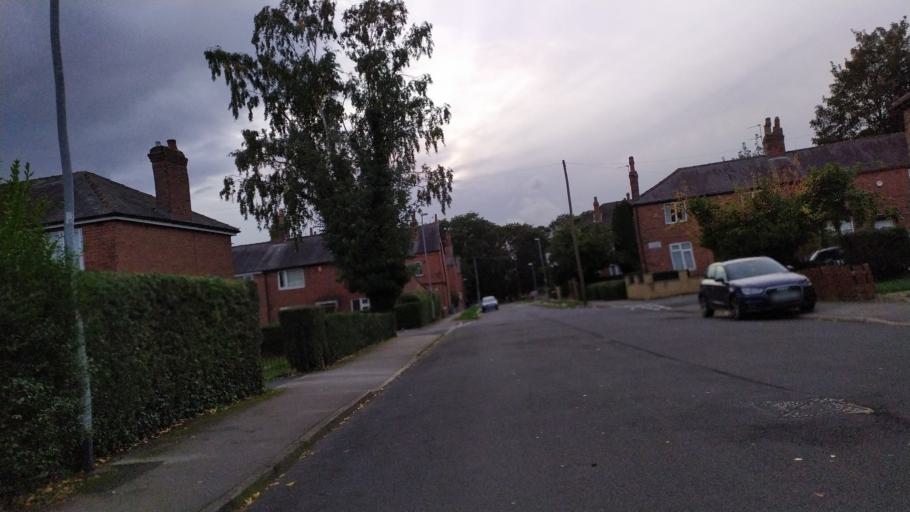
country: GB
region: England
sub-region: City and Borough of Leeds
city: Leeds
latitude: 53.8187
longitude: -1.5875
